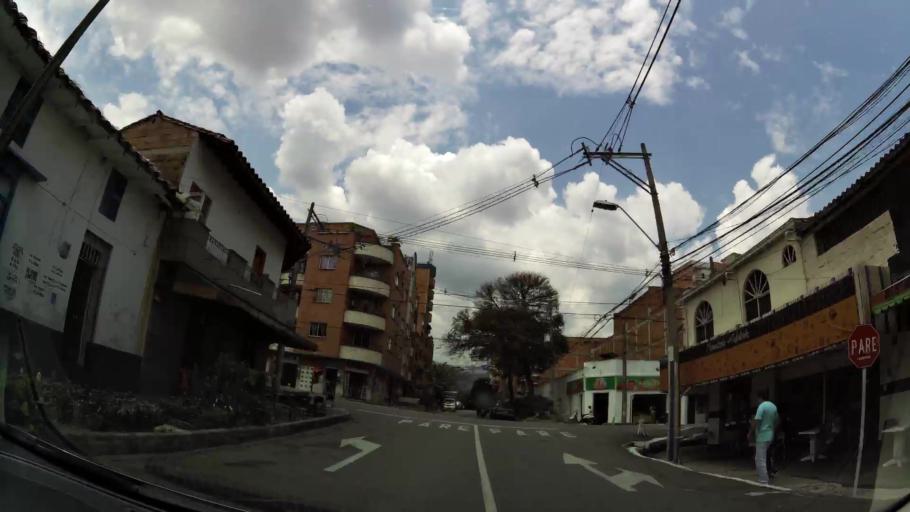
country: CO
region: Antioquia
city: Medellin
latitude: 6.2498
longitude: -75.6070
